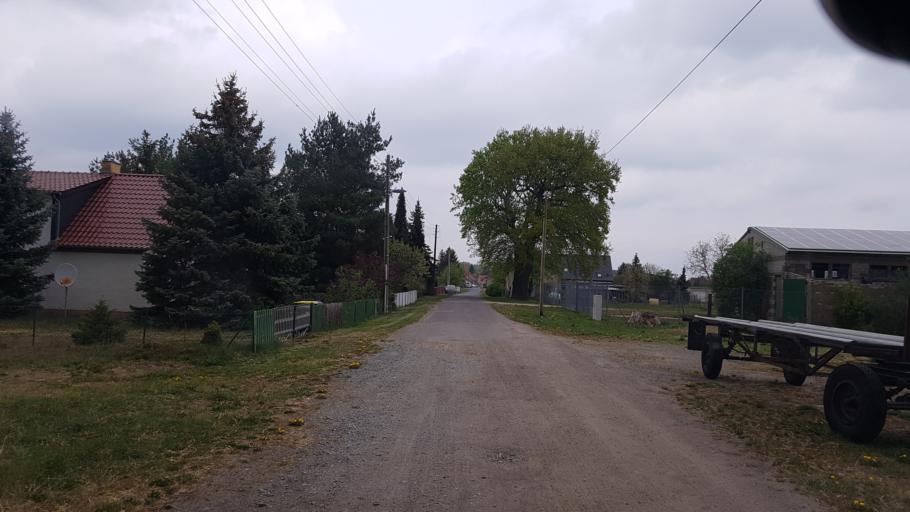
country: DE
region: Brandenburg
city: Sallgast
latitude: 51.5992
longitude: 13.9032
